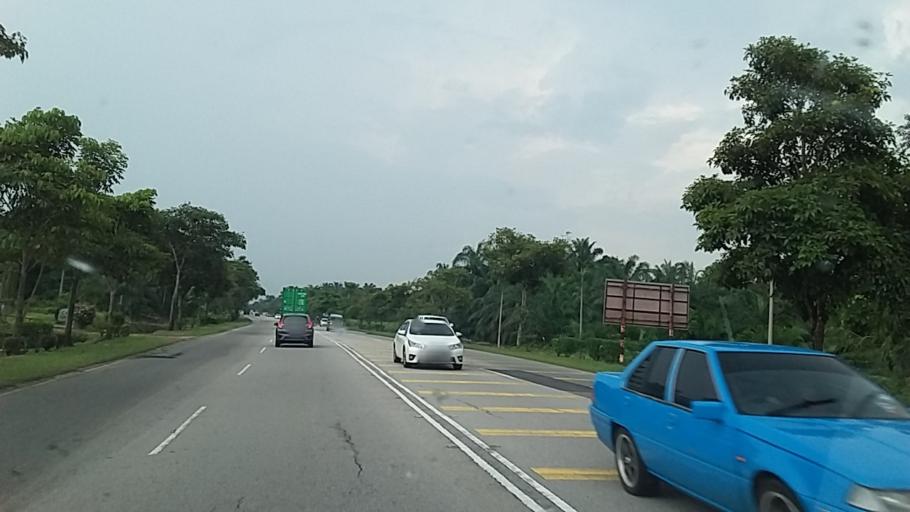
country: MY
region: Johor
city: Parit Raja
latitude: 1.8761
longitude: 103.1426
